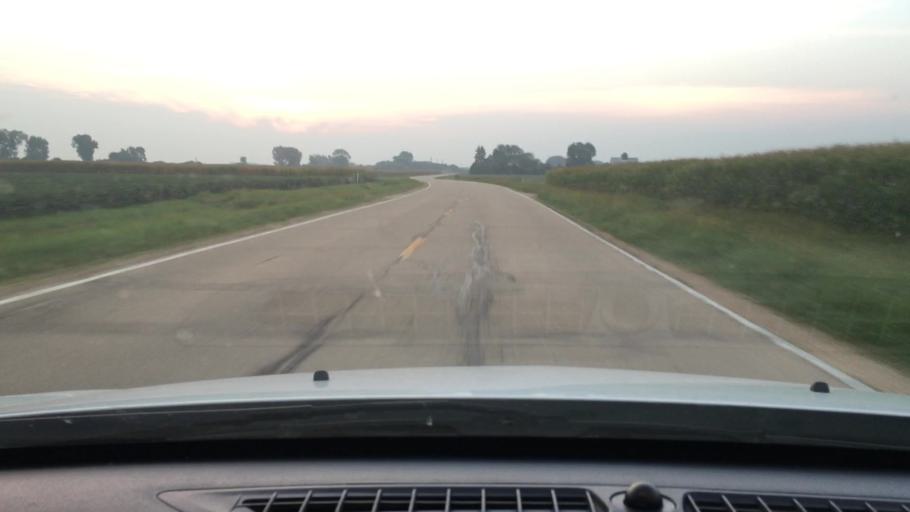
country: US
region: Illinois
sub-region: Ogle County
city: Rochelle
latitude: 41.8470
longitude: -89.0555
